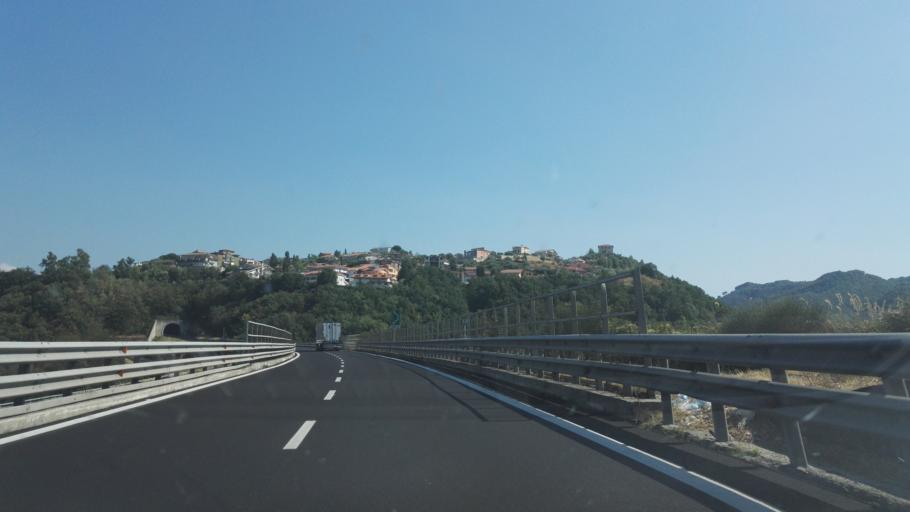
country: IT
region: Calabria
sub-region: Provincia di Cosenza
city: Rosario
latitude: 39.2896
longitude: 16.2390
